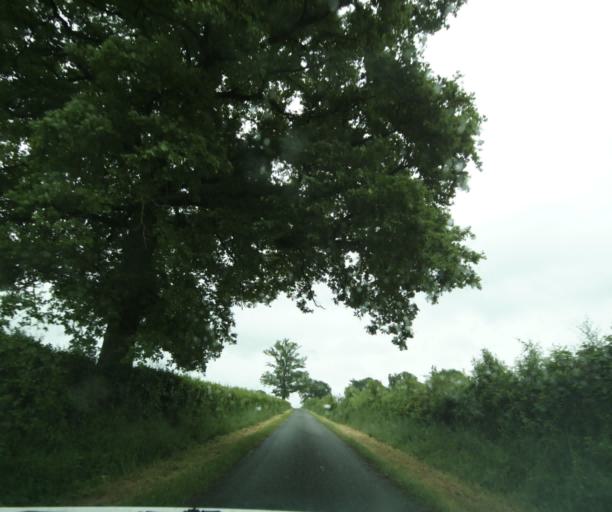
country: FR
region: Bourgogne
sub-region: Departement de Saone-et-Loire
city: Palinges
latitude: 46.4919
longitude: 4.2392
